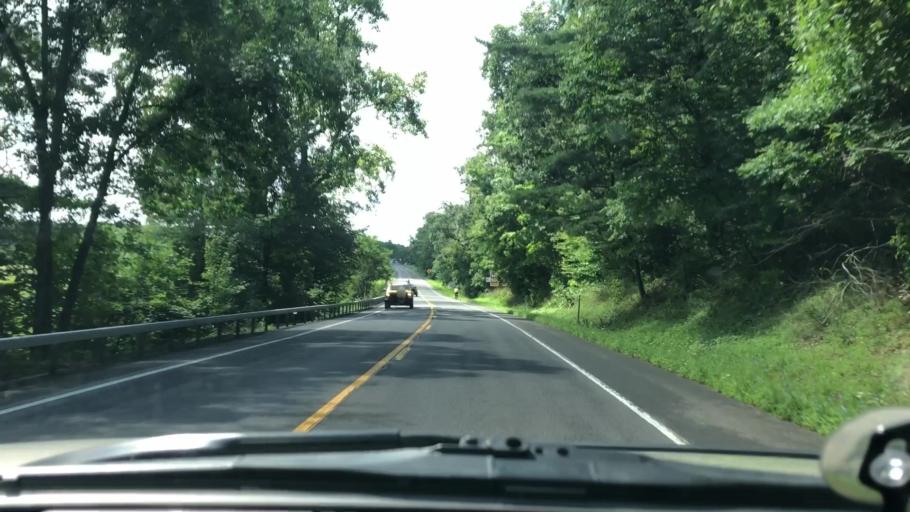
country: US
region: New York
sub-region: Greene County
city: Palenville
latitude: 42.1973
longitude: -73.9861
